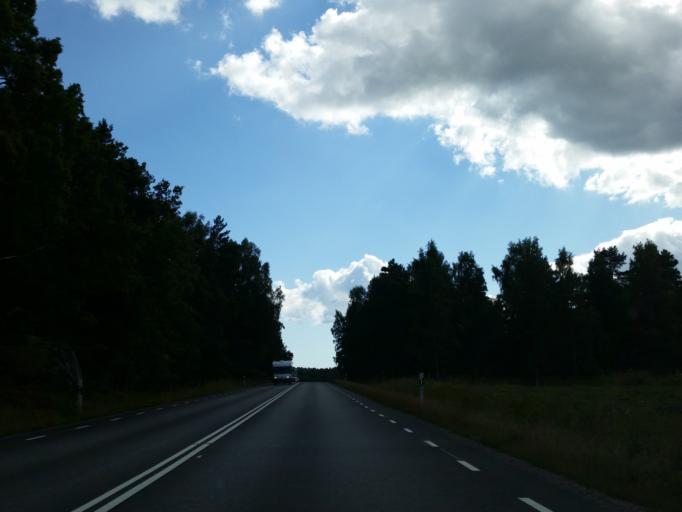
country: SE
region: Soedermanland
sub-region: Trosa Kommun
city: Vagnharad
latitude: 58.9613
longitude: 17.5610
